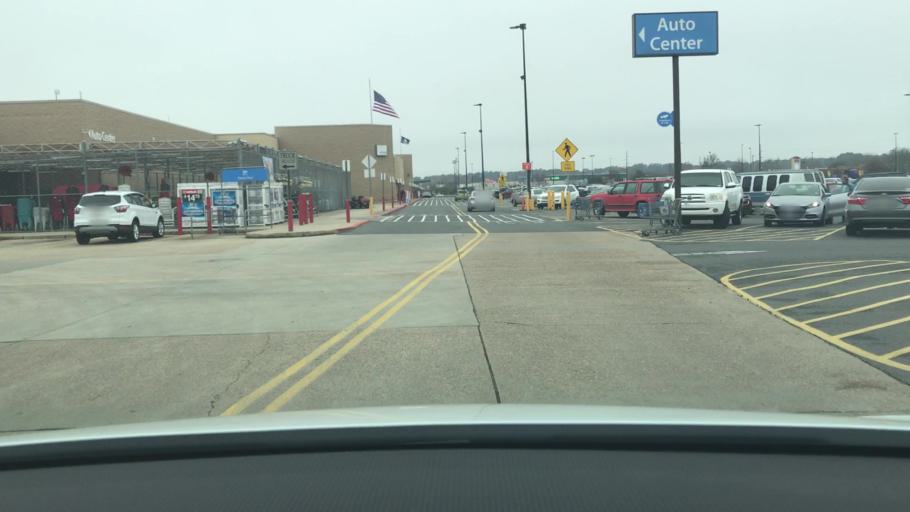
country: US
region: Louisiana
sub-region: Bossier Parish
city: Bossier City
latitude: 32.4296
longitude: -93.7112
